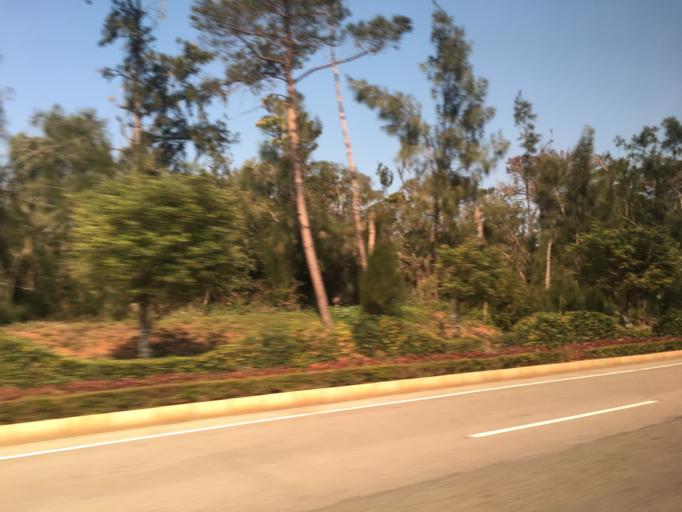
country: TW
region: Fukien
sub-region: Kinmen
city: Jincheng
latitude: 24.4334
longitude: 118.3470
